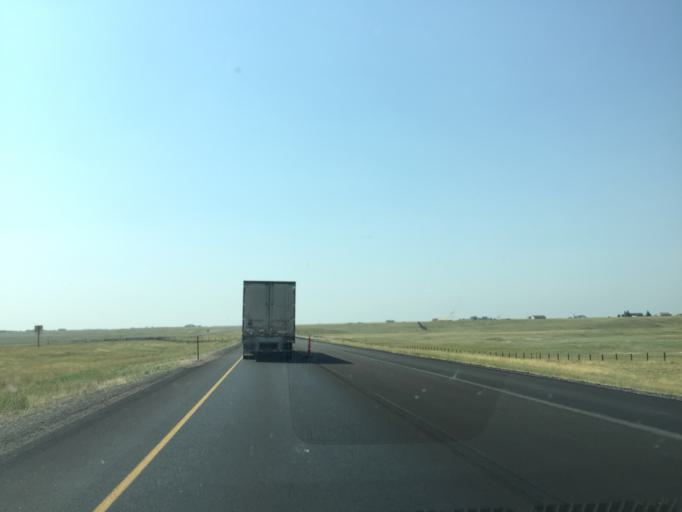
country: US
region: Wyoming
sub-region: Laramie County
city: Ranchettes
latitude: 41.3128
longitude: -104.8584
